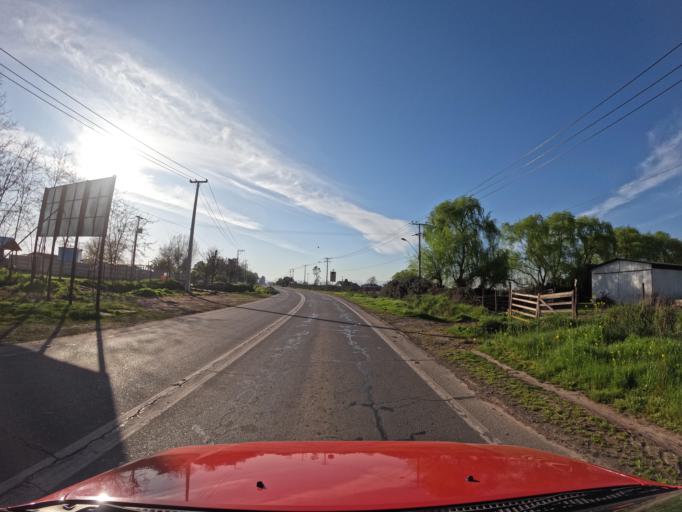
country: CL
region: Maule
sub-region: Provincia de Curico
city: Teno
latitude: -34.8727
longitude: -71.0850
